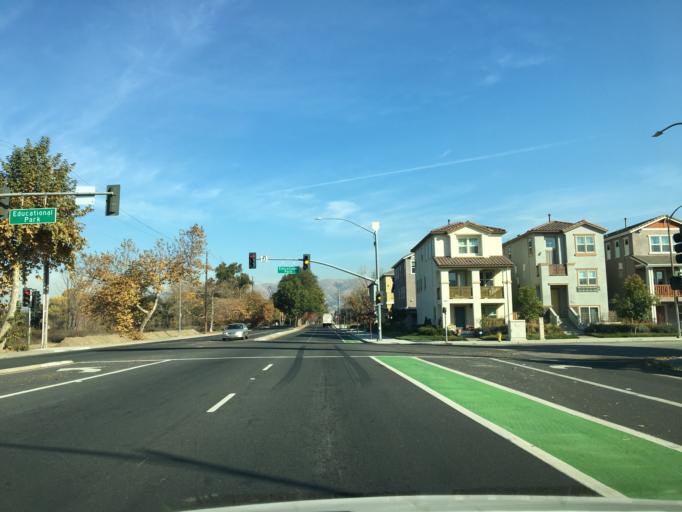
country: US
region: California
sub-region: Santa Clara County
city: Alum Rock
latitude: 37.3706
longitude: -121.8636
